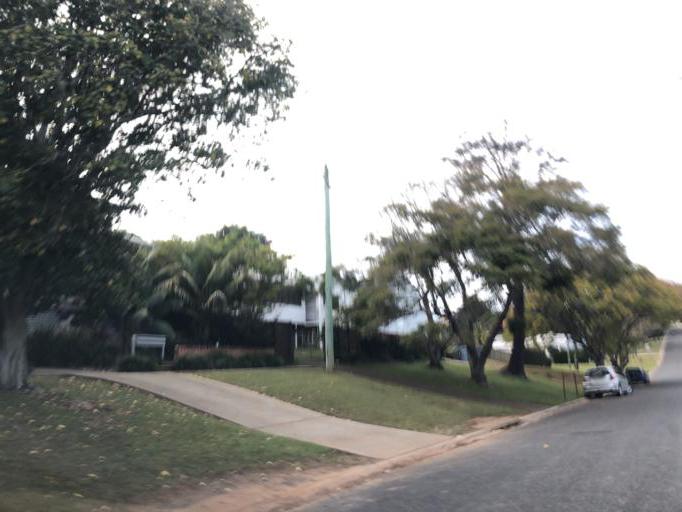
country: AU
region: New South Wales
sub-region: Coffs Harbour
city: Coffs Harbour
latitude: -30.3057
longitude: 153.1337
